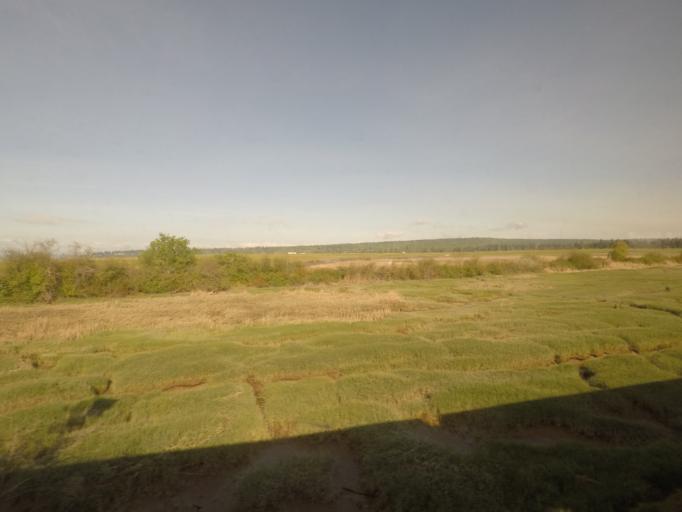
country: US
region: Washington
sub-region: Snohomish County
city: Marysville
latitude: 48.0385
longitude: -122.1833
